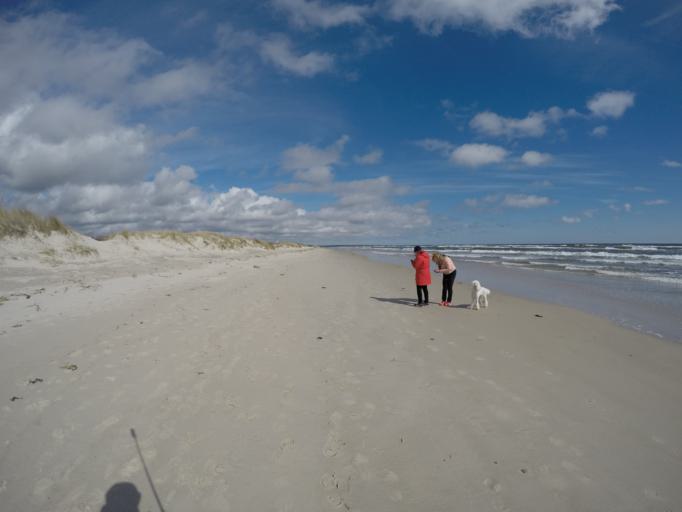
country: SE
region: Skane
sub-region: Simrishamns Kommun
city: Simrishamn
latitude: 55.3985
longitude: 14.2135
